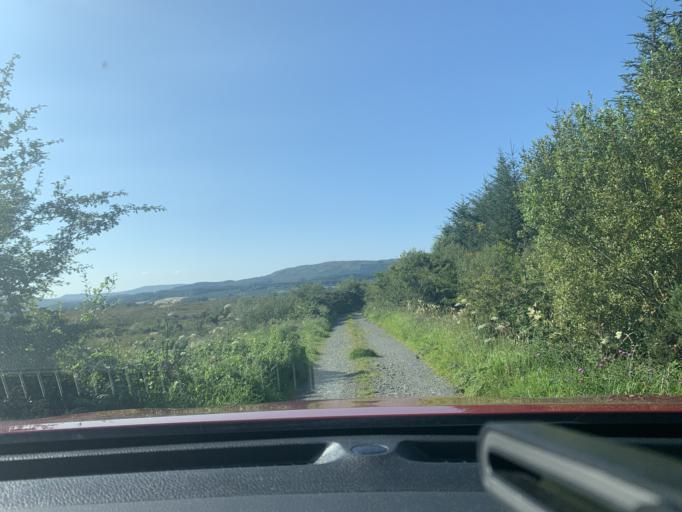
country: IE
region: Connaught
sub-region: Sligo
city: Tobercurry
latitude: 54.0652
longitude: -8.7980
